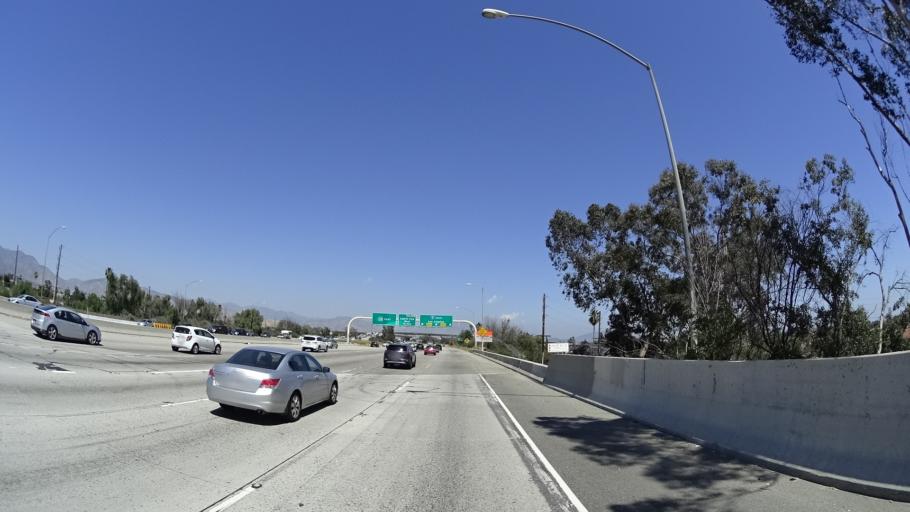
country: US
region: California
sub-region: Los Angeles County
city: San Fernando
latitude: 34.2656
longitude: -118.4504
